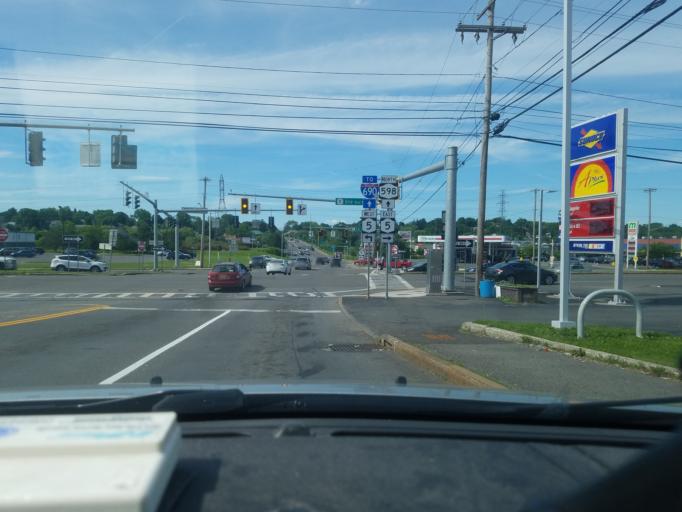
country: US
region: New York
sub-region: Onondaga County
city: East Syracuse
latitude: 43.0532
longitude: -76.1040
